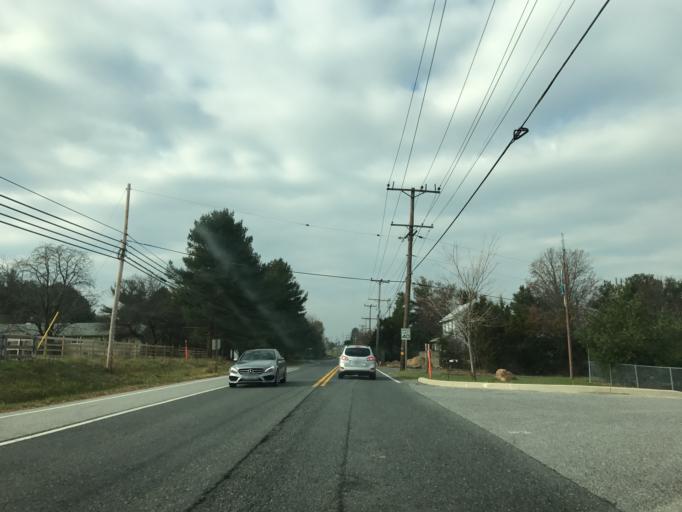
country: US
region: Maryland
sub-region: Harford County
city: Jarrettsville
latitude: 39.6129
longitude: -76.5088
